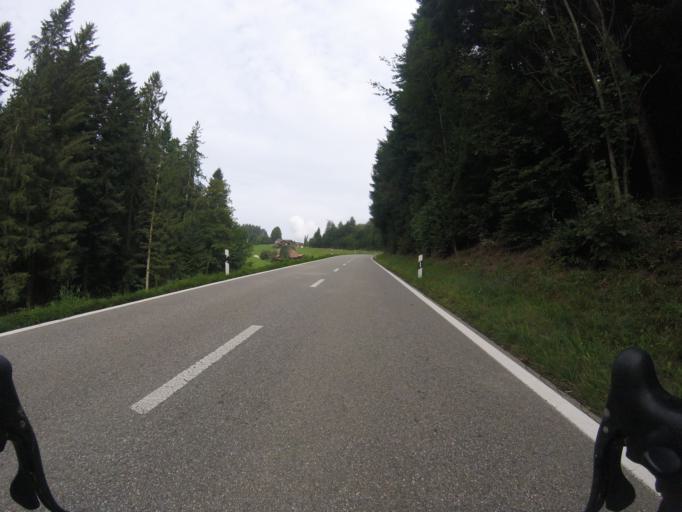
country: CH
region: Bern
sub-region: Bern-Mittelland District
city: Walkringen
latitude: 46.9444
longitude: 7.6512
